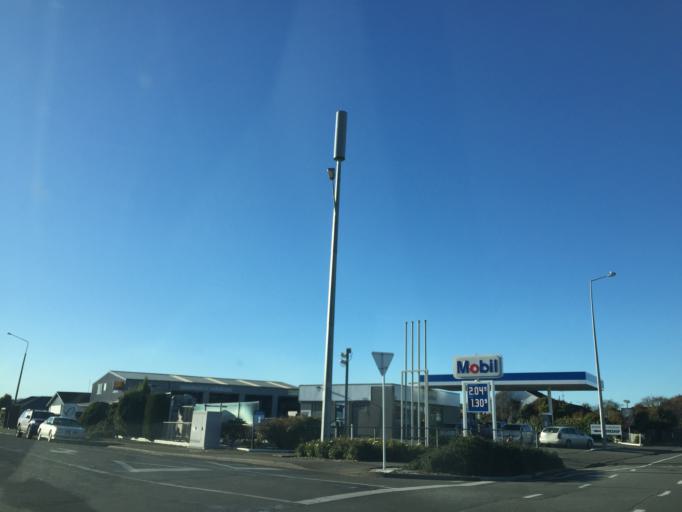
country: NZ
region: Southland
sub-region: Invercargill City
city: Invercargill
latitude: -46.4032
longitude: 168.3645
